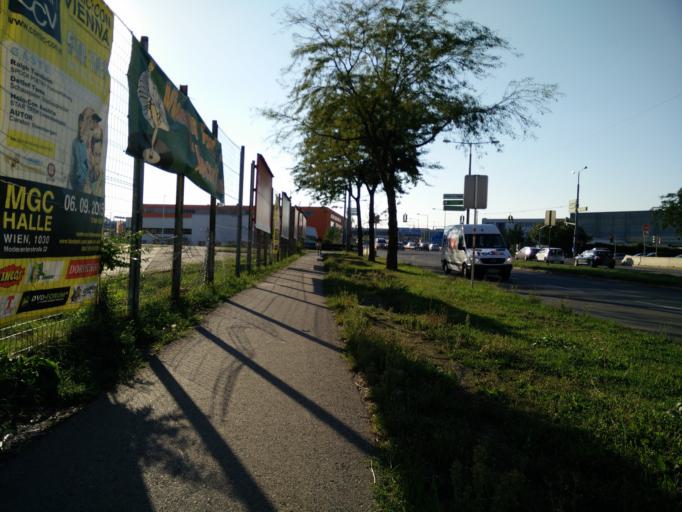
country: AT
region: Vienna
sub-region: Wien Stadt
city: Vienna
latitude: 48.1856
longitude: 16.4140
